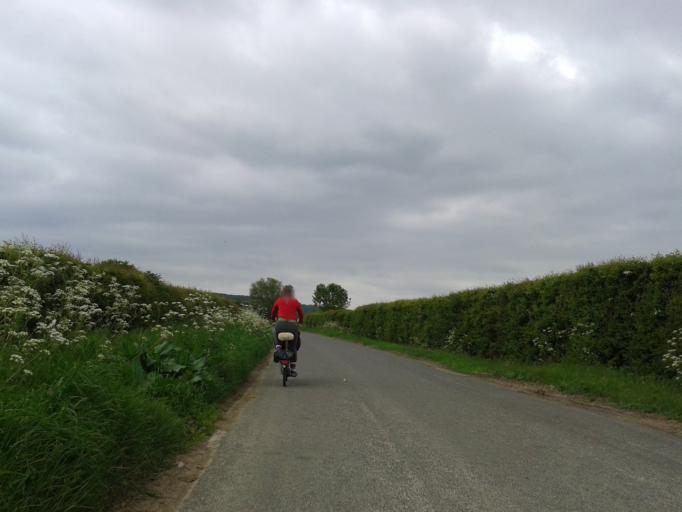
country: GB
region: England
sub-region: Northamptonshire
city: Corby
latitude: 52.5329
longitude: -0.6942
